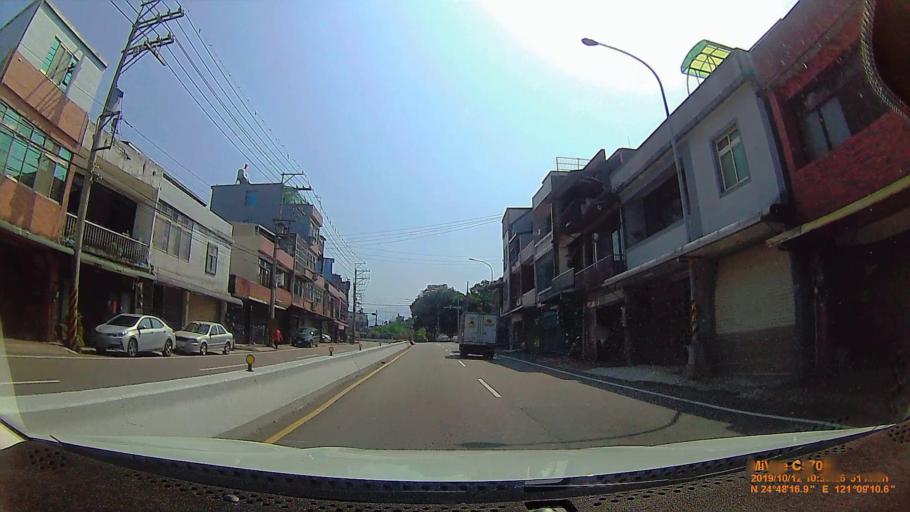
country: TW
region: Taiwan
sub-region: Hsinchu
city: Zhubei
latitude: 24.8047
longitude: 121.1530
